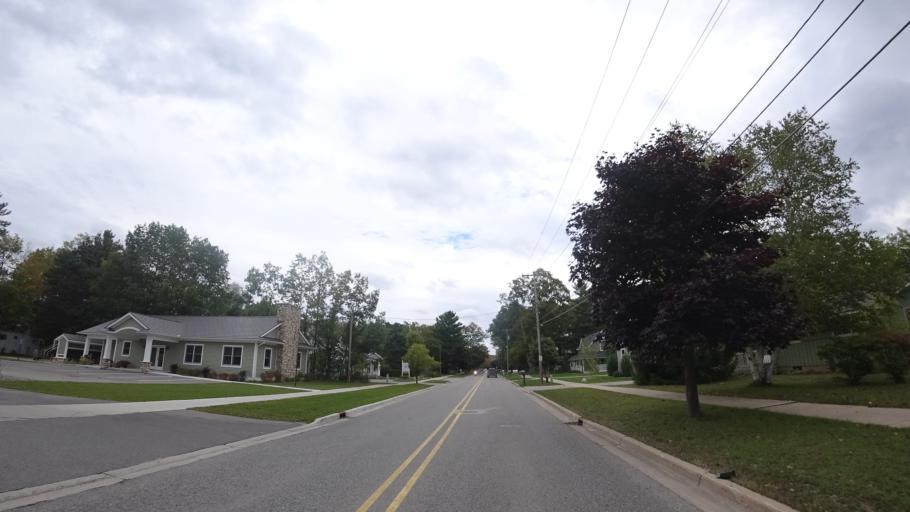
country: US
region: Michigan
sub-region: Emmet County
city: Harbor Springs
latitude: 45.4354
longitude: -84.9789
